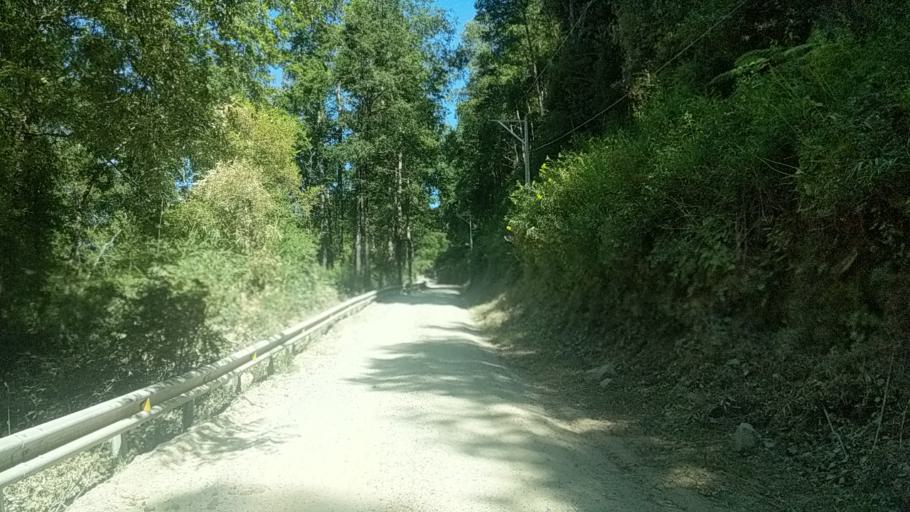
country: CL
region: Araucania
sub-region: Provincia de Cautin
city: Pucon
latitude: -39.0635
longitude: -71.7217
